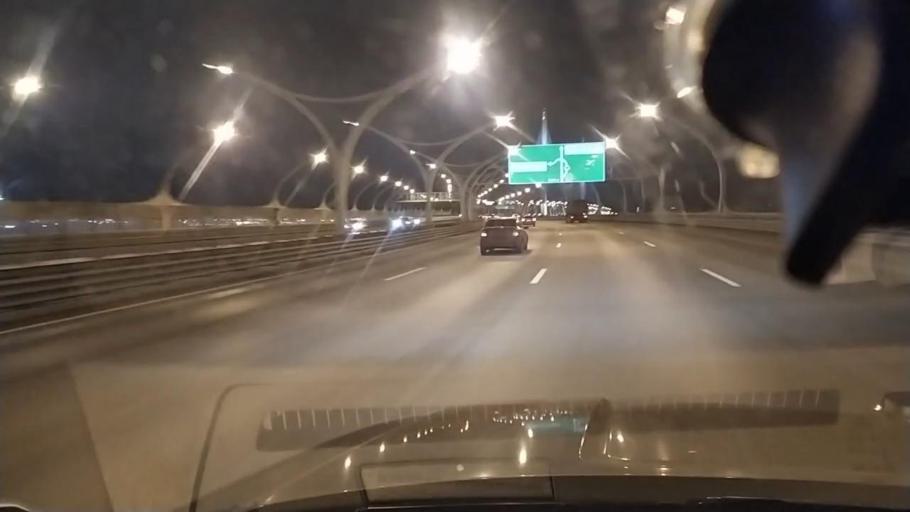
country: RU
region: St.-Petersburg
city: Staraya Derevnya
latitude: 59.9731
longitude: 30.2131
